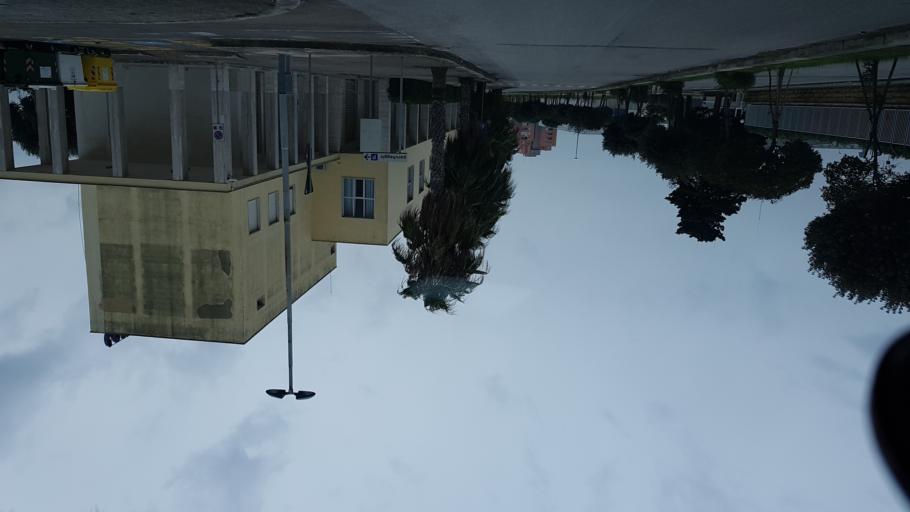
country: IT
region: Apulia
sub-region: Provincia di Brindisi
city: Brindisi
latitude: 40.6364
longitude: 17.9544
